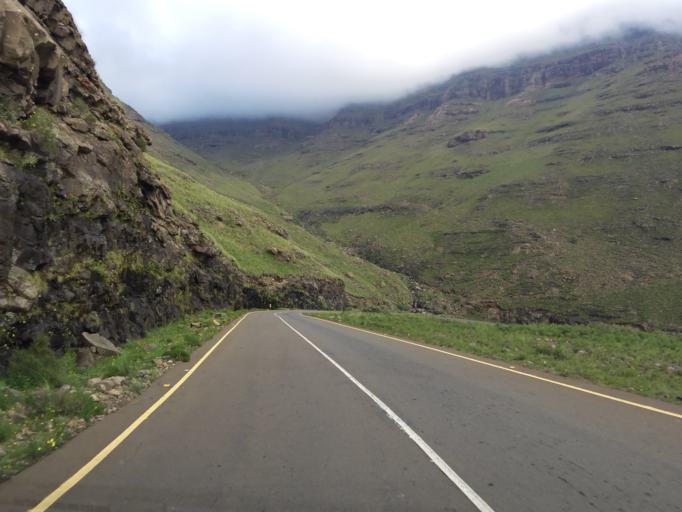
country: LS
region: Butha-Buthe
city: Butha-Buthe
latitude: -29.0713
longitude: 28.3813
